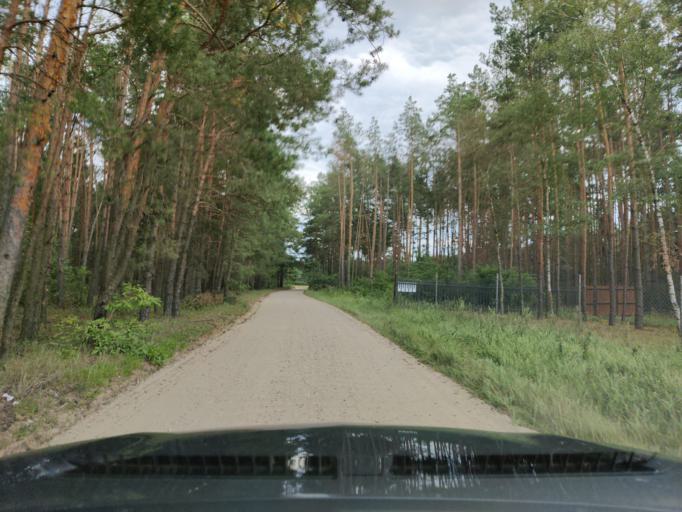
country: PL
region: Masovian Voivodeship
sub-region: Powiat pultuski
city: Pultusk
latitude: 52.7613
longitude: 21.1344
